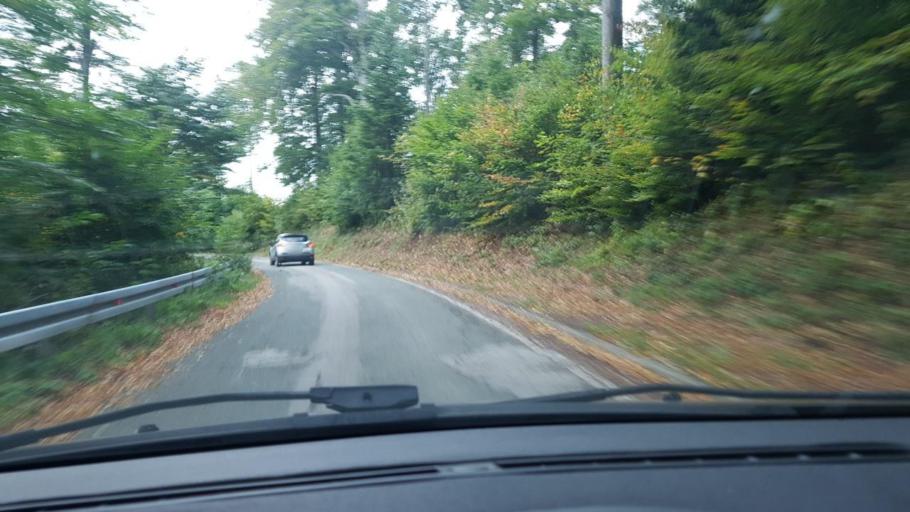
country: HR
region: Grad Zagreb
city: Kasina
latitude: 45.8861
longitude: 15.9317
